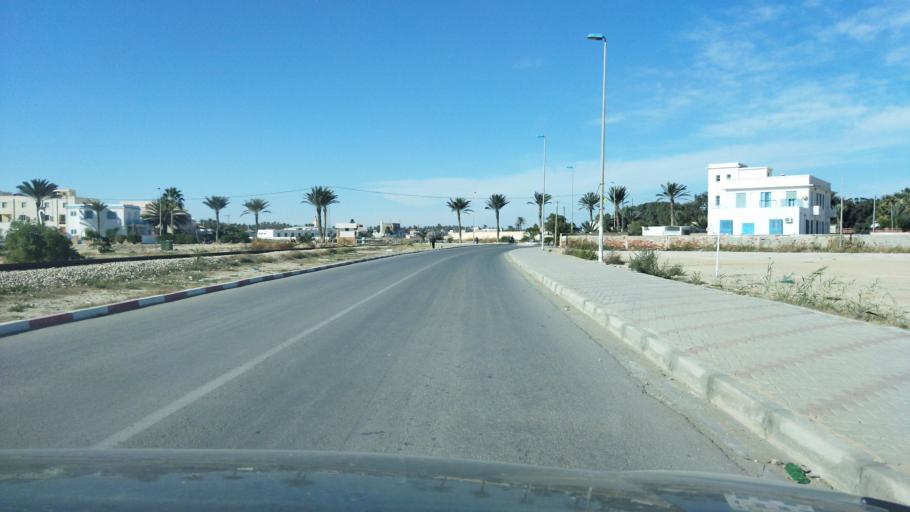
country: TN
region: Qabis
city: Gabes
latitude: 33.8900
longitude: 10.1143
